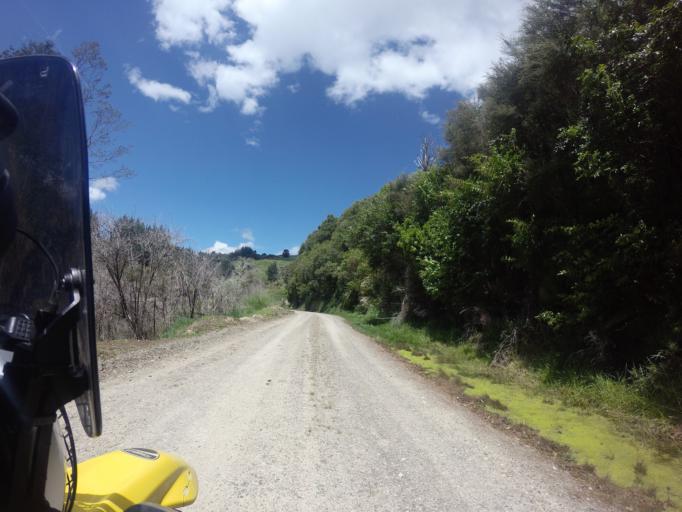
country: NZ
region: Hawke's Bay
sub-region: Wairoa District
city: Wairoa
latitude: -38.9724
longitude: 177.6748
